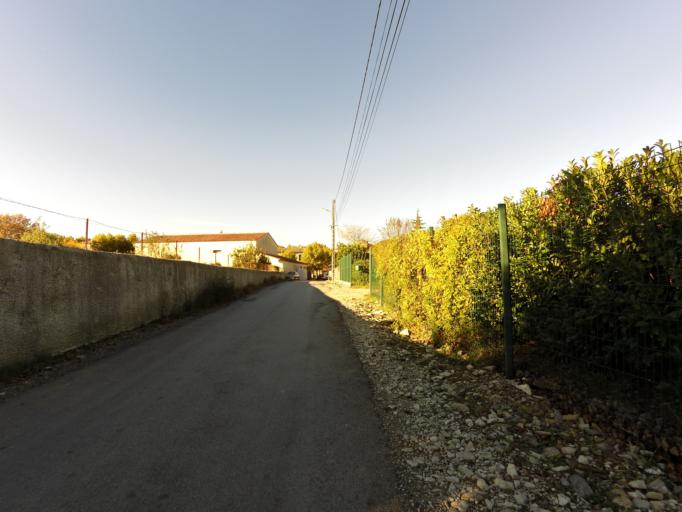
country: FR
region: Languedoc-Roussillon
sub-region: Departement du Gard
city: Sauve
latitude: 43.9883
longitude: 3.9556
